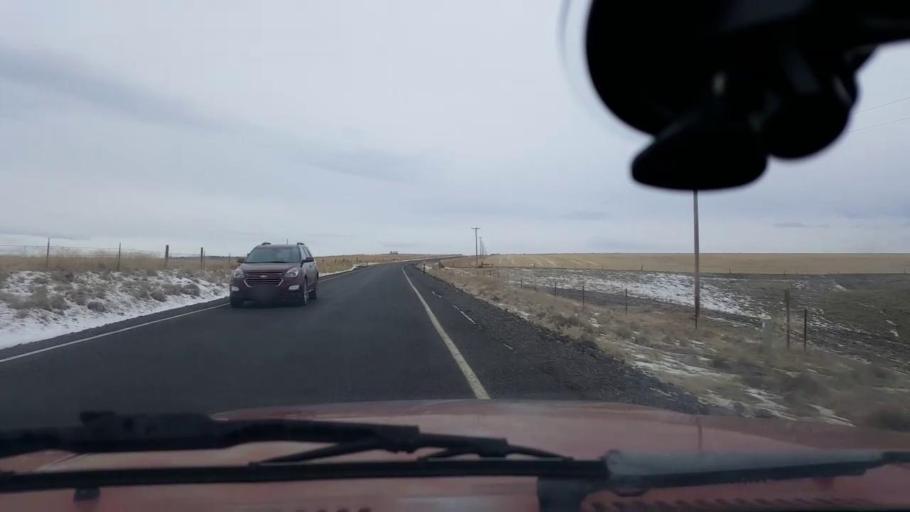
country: US
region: Washington
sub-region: Garfield County
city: Pomeroy
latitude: 46.3230
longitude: -117.3701
